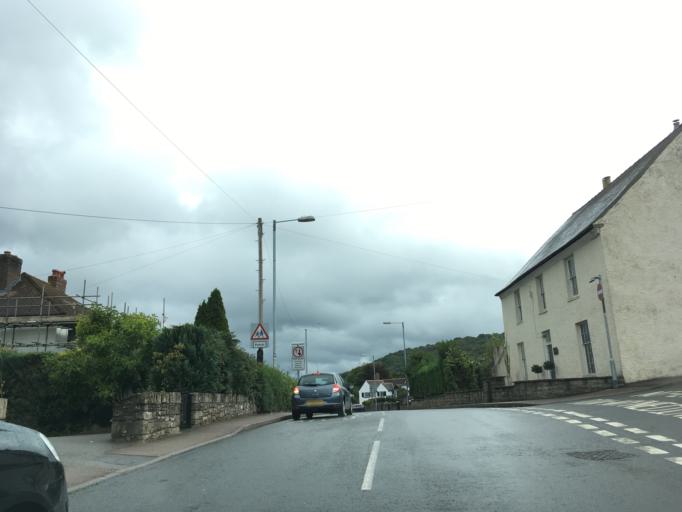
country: GB
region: Wales
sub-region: Monmouthshire
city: Gilwern
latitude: 51.8186
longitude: -3.0661
